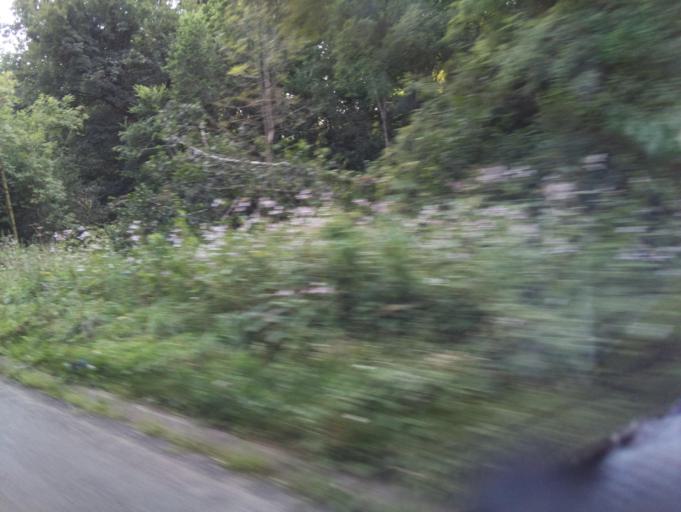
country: GB
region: England
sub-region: Devon
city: Tiverton
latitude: 50.8828
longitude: -3.4913
